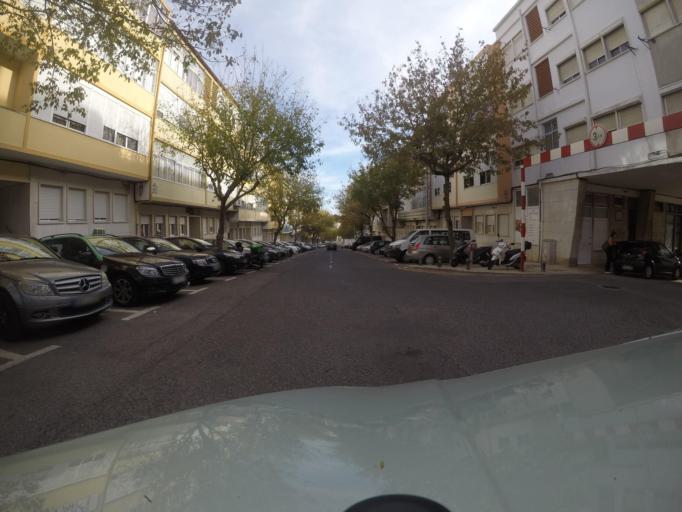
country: PT
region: Lisbon
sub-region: Amadora
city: Amadora
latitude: 38.7595
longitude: -9.2258
